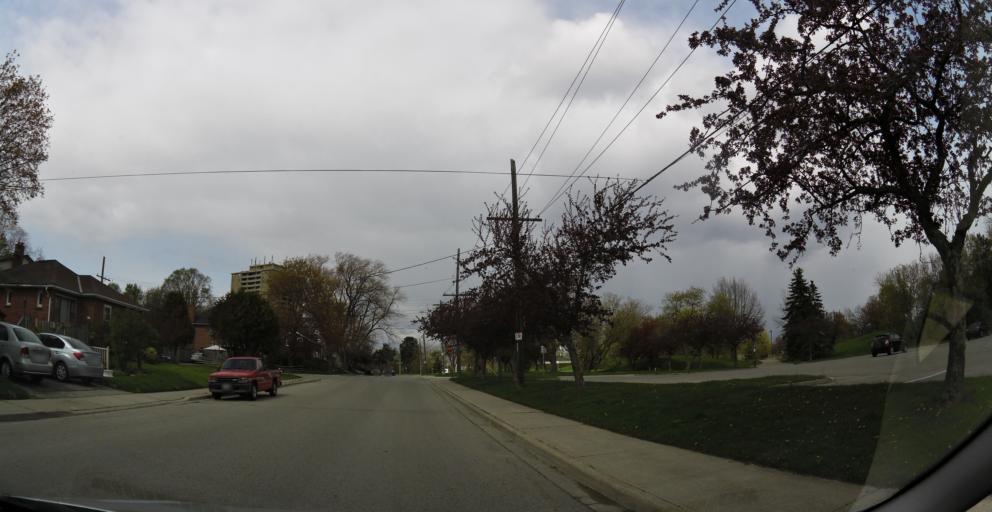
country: CA
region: Ontario
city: Mississauga
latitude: 43.5463
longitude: -79.5857
